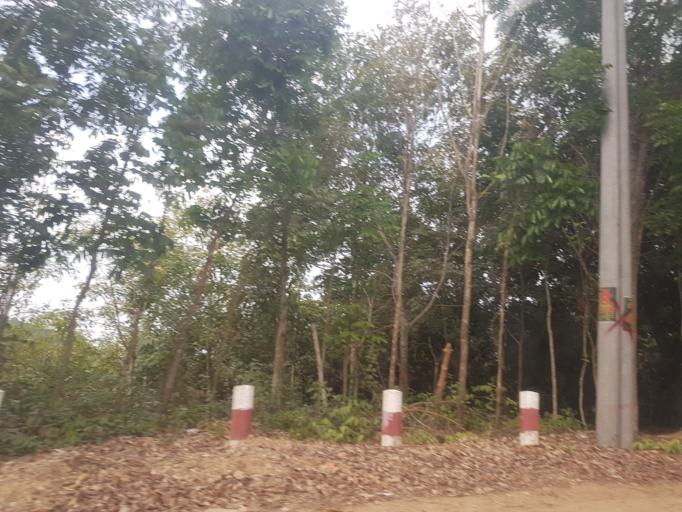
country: MM
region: Ayeyarwady
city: Pathein
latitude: 16.9447
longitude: 94.5720
